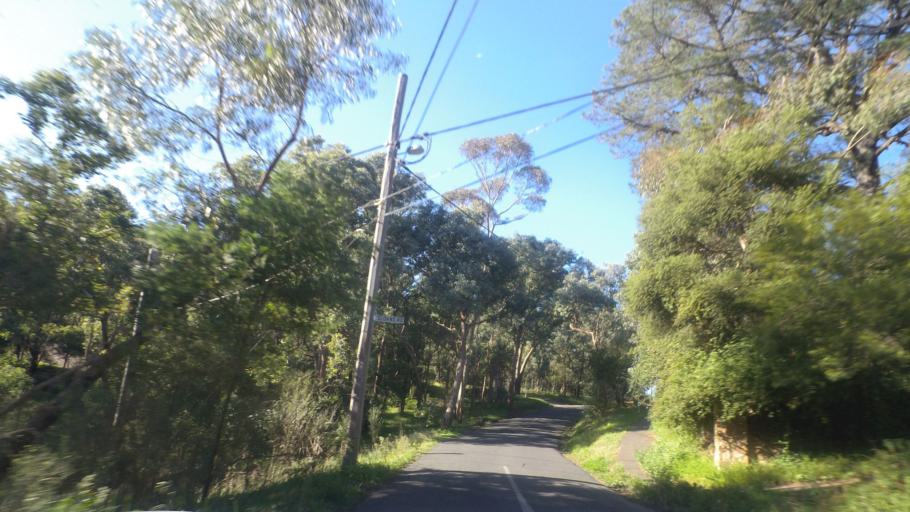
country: AU
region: Victoria
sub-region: Nillumbik
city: North Warrandyte
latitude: -37.7198
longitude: 145.2212
